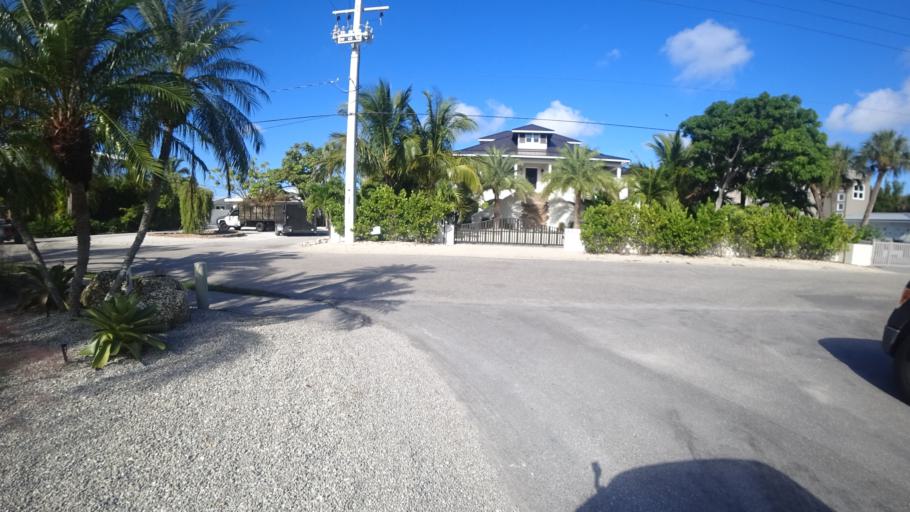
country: US
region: Florida
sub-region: Manatee County
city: Anna Maria
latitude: 27.5285
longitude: -82.7238
